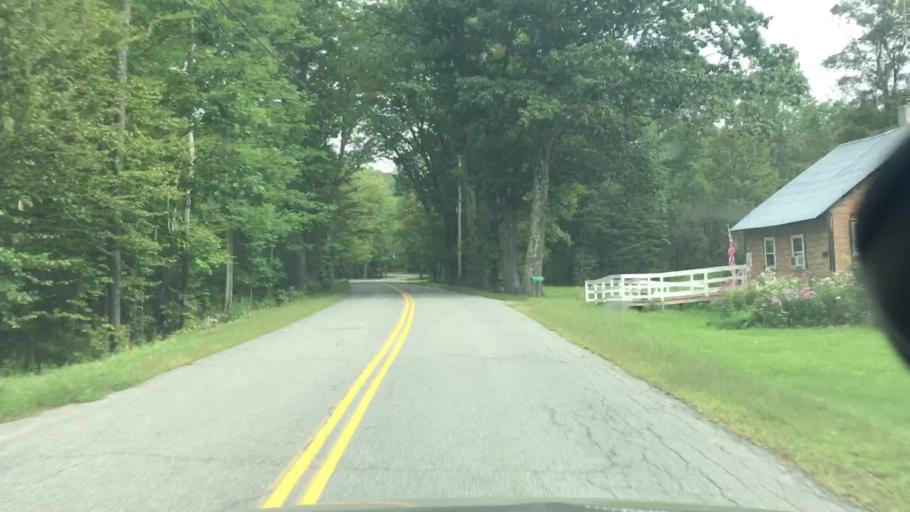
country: US
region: Massachusetts
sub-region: Franklin County
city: Colrain
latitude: 42.7919
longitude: -72.7675
